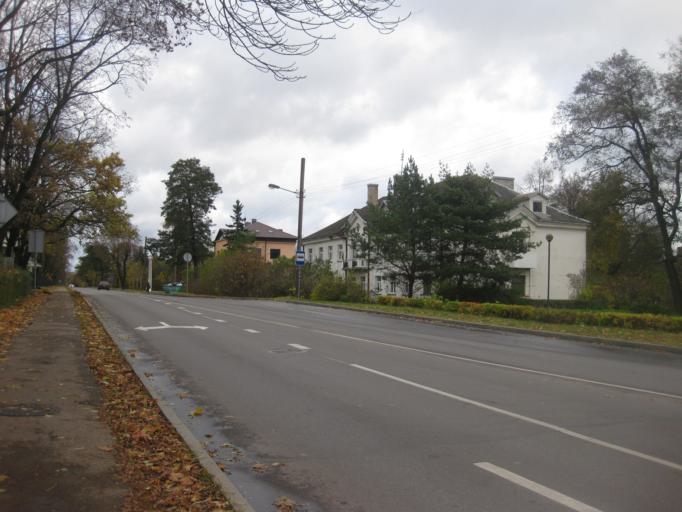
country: LT
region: Kauno apskritis
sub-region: Kaunas
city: Eiguliai
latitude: 54.9065
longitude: 23.9315
